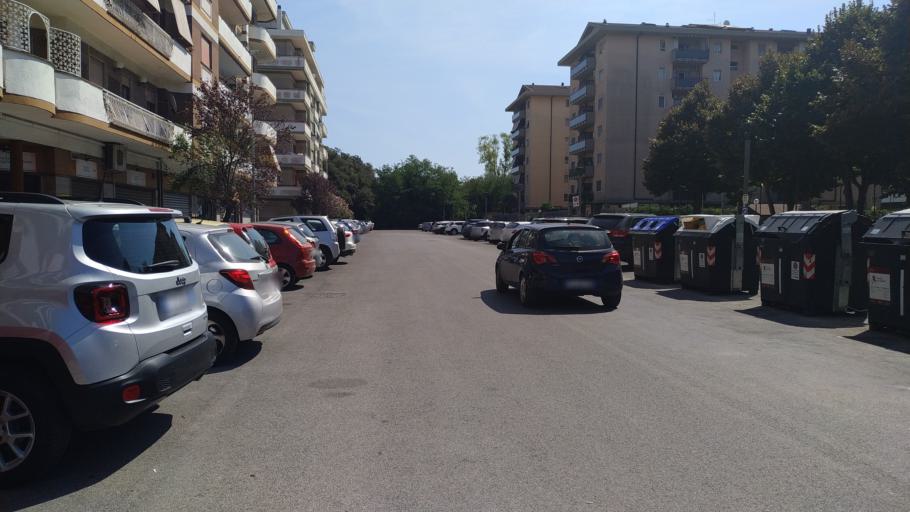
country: IT
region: Latium
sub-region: Citta metropolitana di Roma Capitale
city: Lido di Ostia
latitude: 41.7315
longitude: 12.3042
